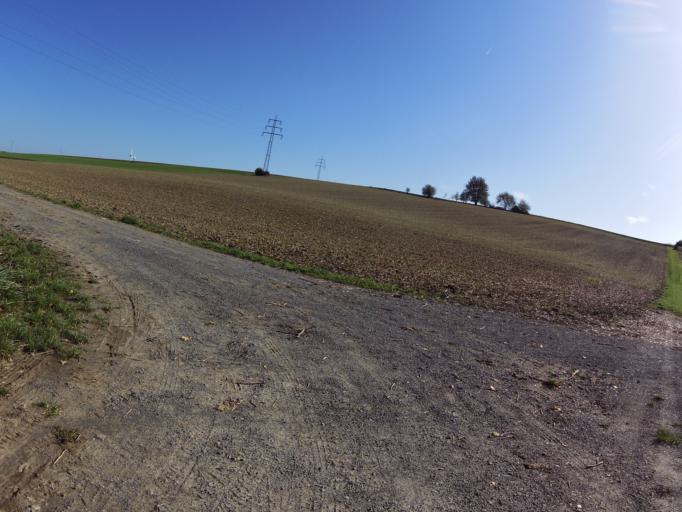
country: DE
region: Bavaria
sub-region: Regierungsbezirk Unterfranken
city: Biebelried
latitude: 49.7591
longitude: 10.0651
